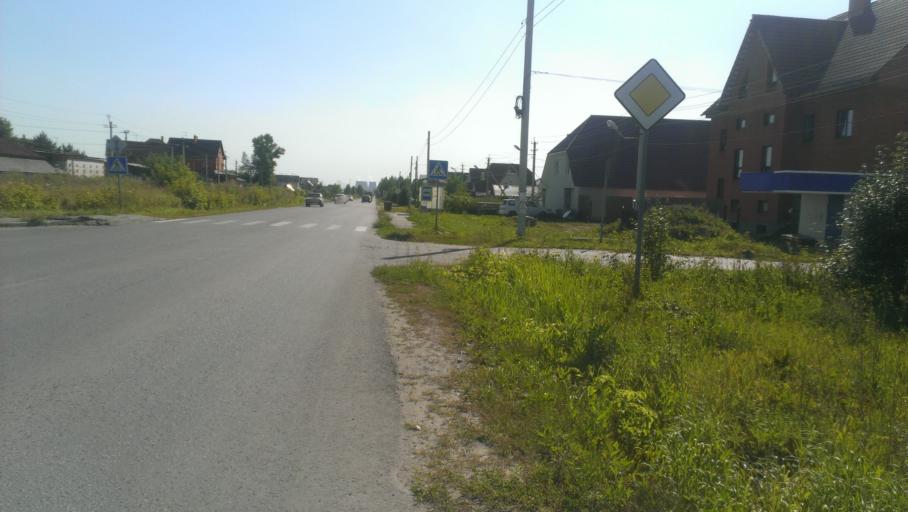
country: RU
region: Altai Krai
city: Novosilikatnyy
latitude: 53.3668
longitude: 83.6476
